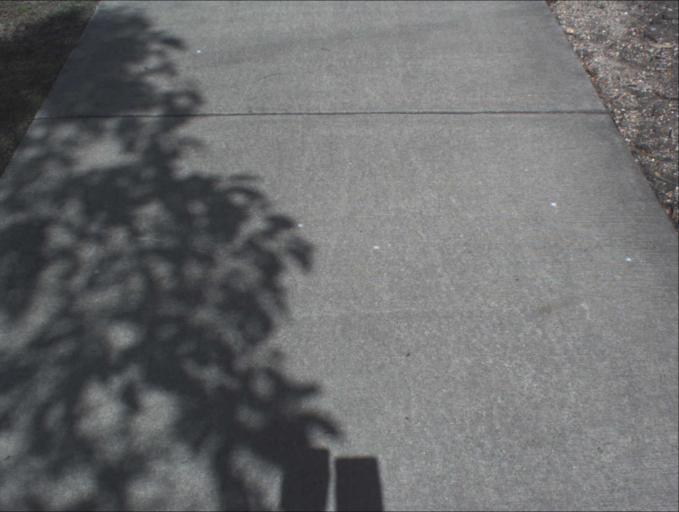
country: AU
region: Queensland
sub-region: Logan
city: Woodridge
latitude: -27.6608
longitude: 153.0813
